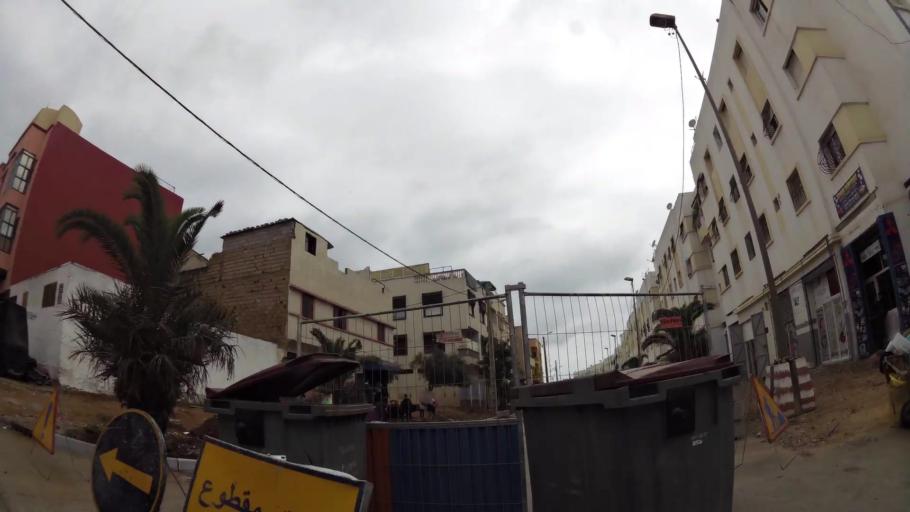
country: MA
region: Rabat-Sale-Zemmour-Zaer
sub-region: Rabat
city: Rabat
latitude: 33.9818
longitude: -6.8155
